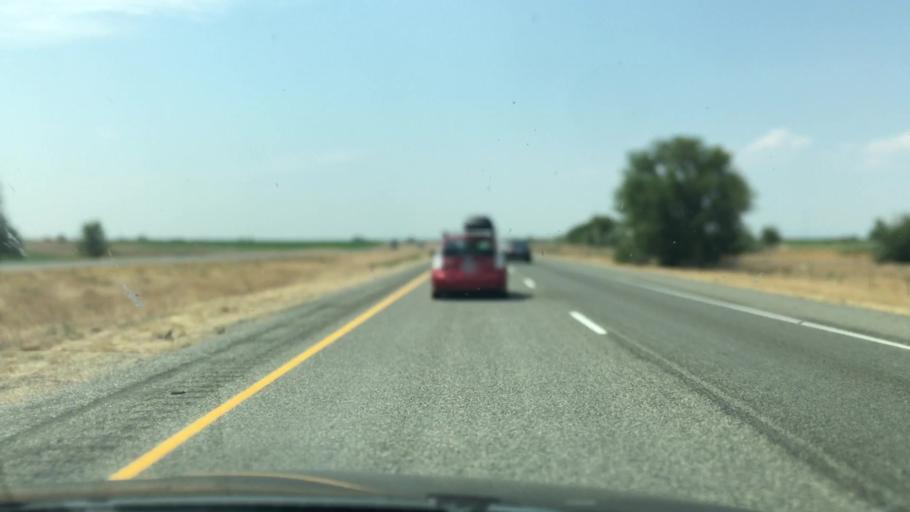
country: US
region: Idaho
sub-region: Gooding County
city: Wendell
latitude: 42.7857
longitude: -114.7379
